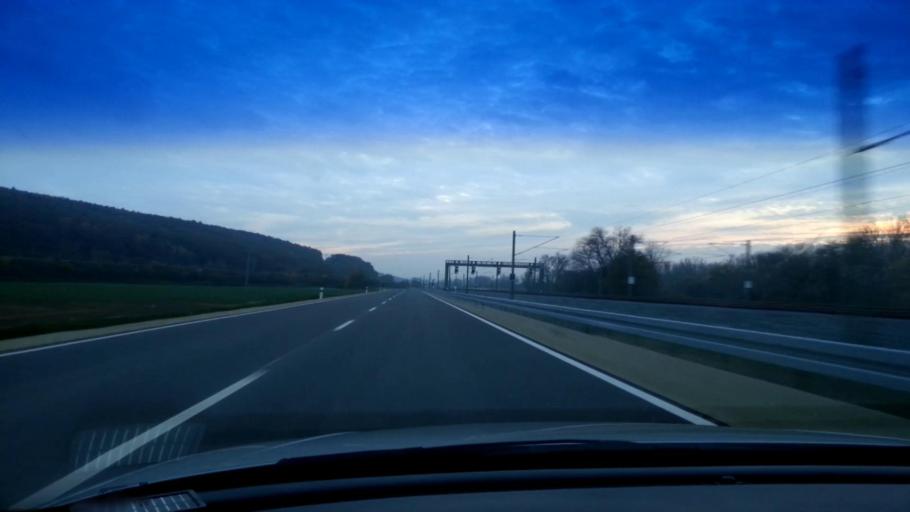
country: DE
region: Bavaria
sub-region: Upper Franconia
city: Zapfendorf
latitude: 50.0042
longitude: 10.9170
